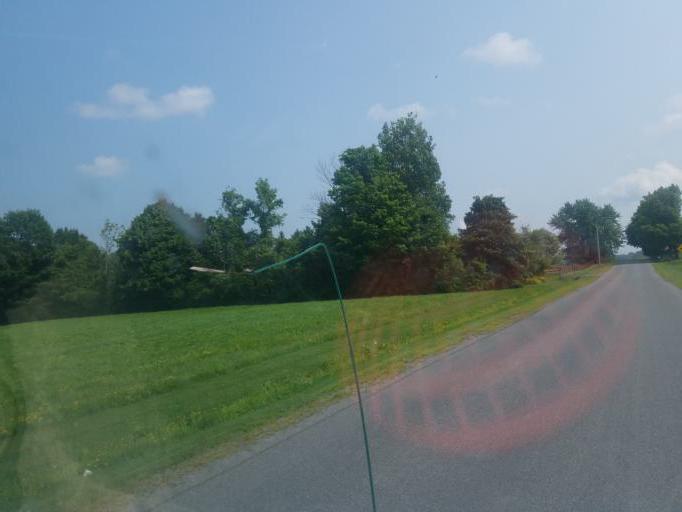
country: US
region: New York
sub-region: Montgomery County
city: Wellsville
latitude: 42.8540
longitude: -74.3523
